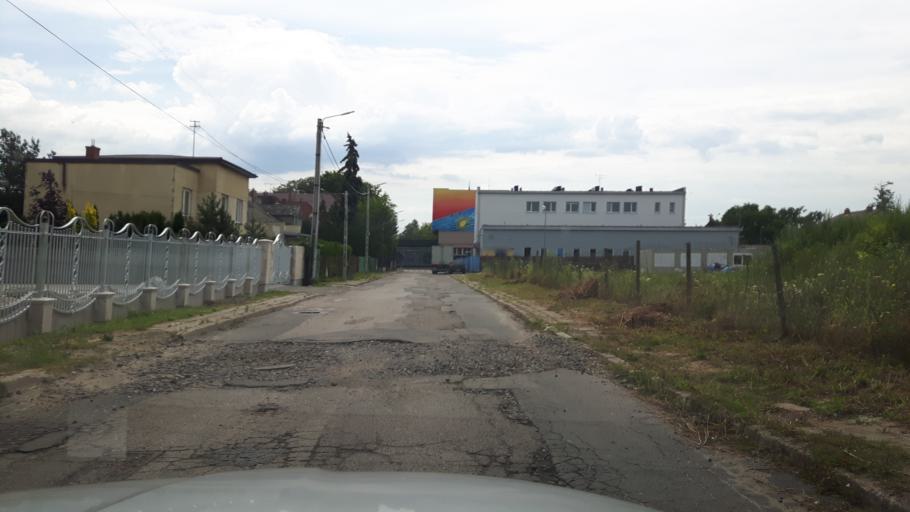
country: PL
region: Masovian Voivodeship
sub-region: Powiat wolominski
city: Wolomin
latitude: 52.3496
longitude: 21.2463
